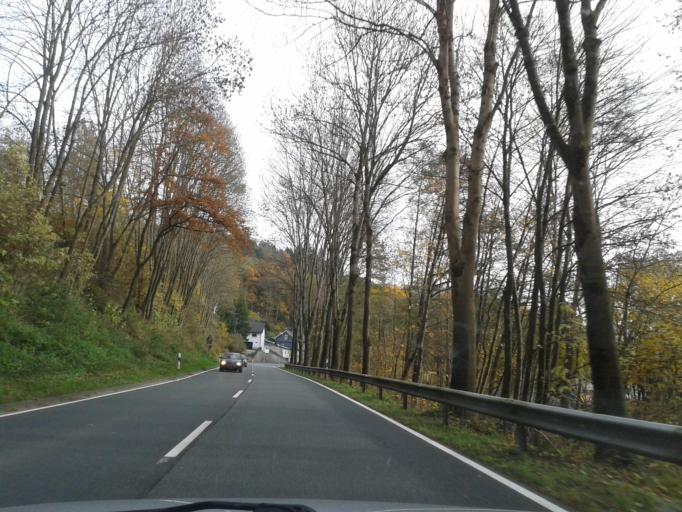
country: DE
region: North Rhine-Westphalia
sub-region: Regierungsbezirk Arnsberg
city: Bad Laasphe
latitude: 50.9239
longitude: 8.3984
